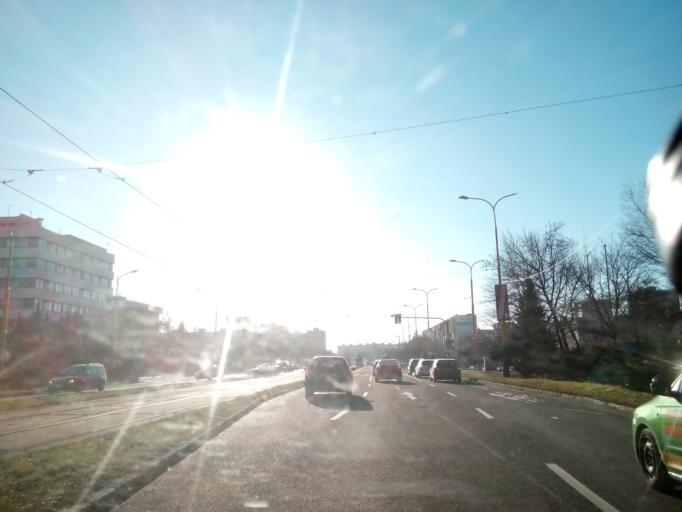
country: SK
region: Kosicky
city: Kosice
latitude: 48.7159
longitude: 21.2345
